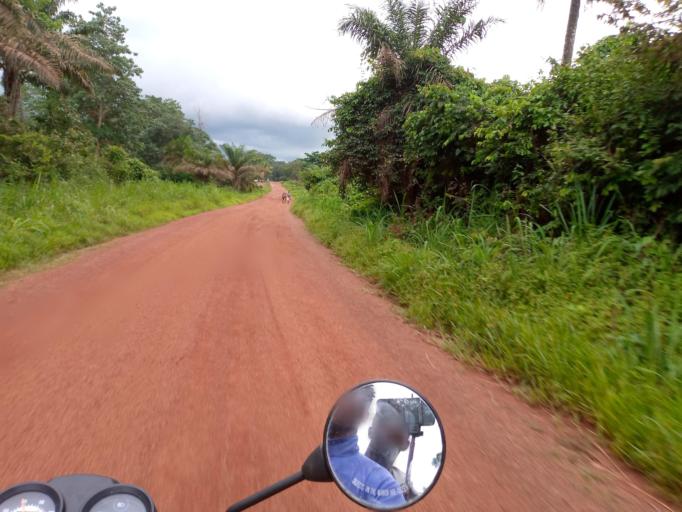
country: SL
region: Northern Province
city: Port Loko
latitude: 8.8841
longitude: -12.7236
